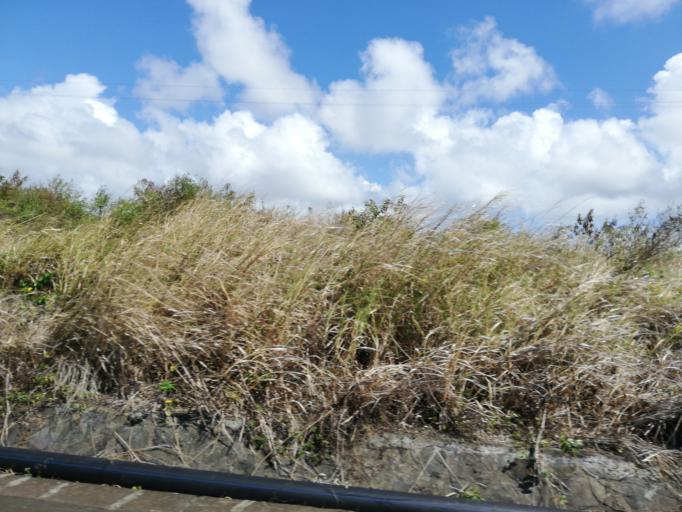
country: MU
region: Riviere du Rempart
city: Goodlands
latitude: -20.0394
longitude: 57.6354
